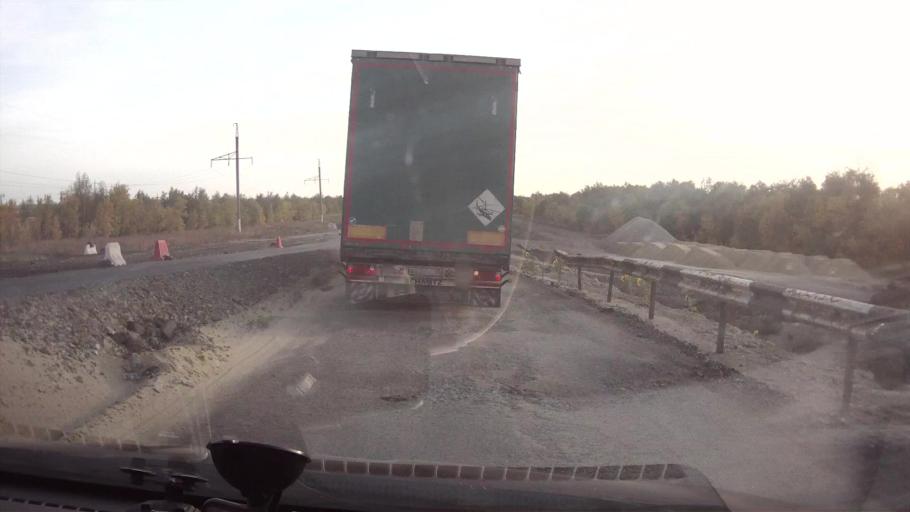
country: RU
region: Saratov
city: Krasnyy Oktyabr'
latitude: 51.3051
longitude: 45.6932
